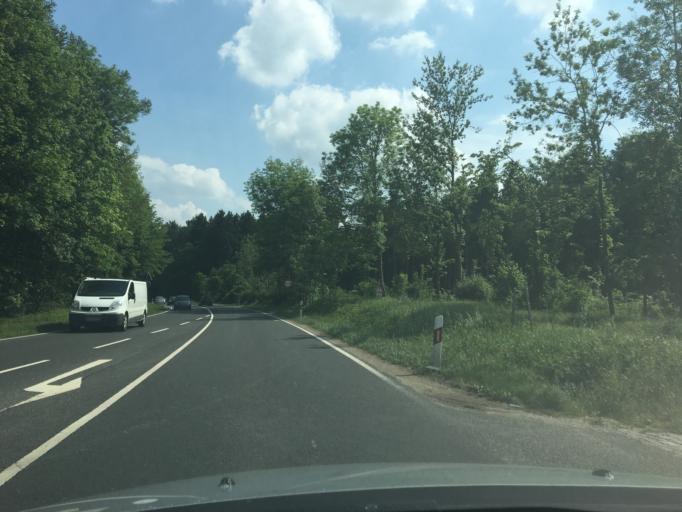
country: DE
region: Bavaria
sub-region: Upper Bavaria
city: Haimhausen
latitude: 48.3039
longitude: 11.5724
